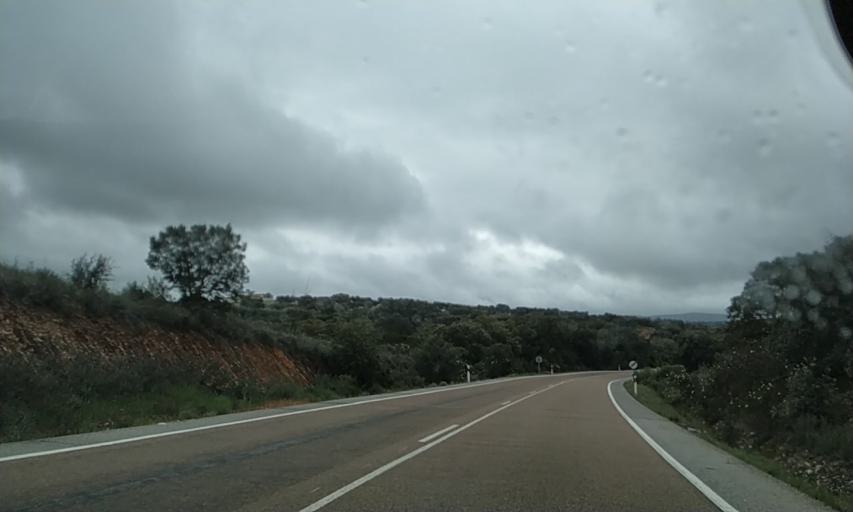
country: ES
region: Extremadura
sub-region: Provincia de Badajoz
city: Puebla de Obando
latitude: 39.2584
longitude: -6.5531
